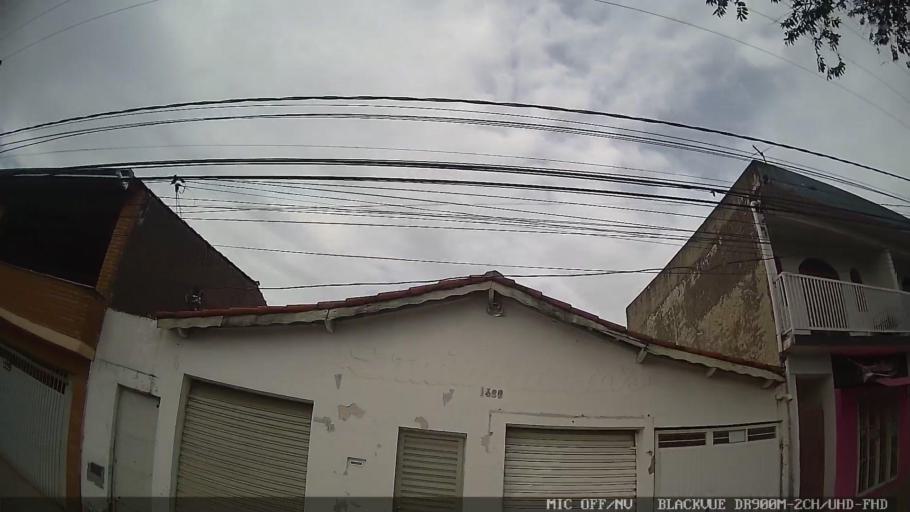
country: BR
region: Sao Paulo
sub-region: Salto
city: Salto
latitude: -23.2216
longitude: -47.2662
